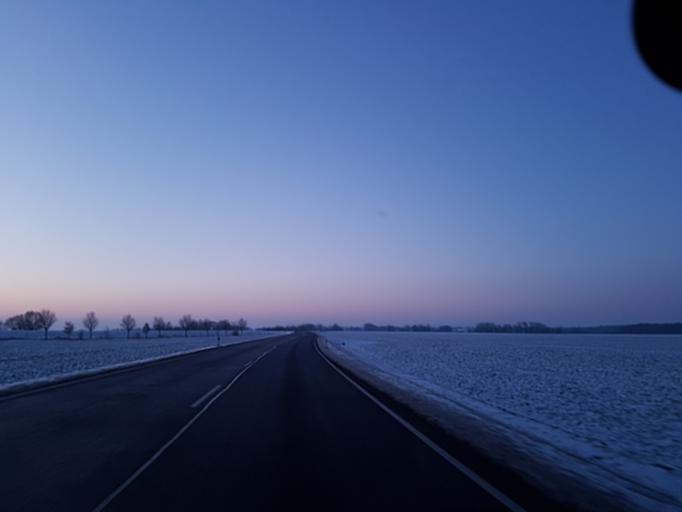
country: DE
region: Brandenburg
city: Muhlberg
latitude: 51.4348
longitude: 13.1861
